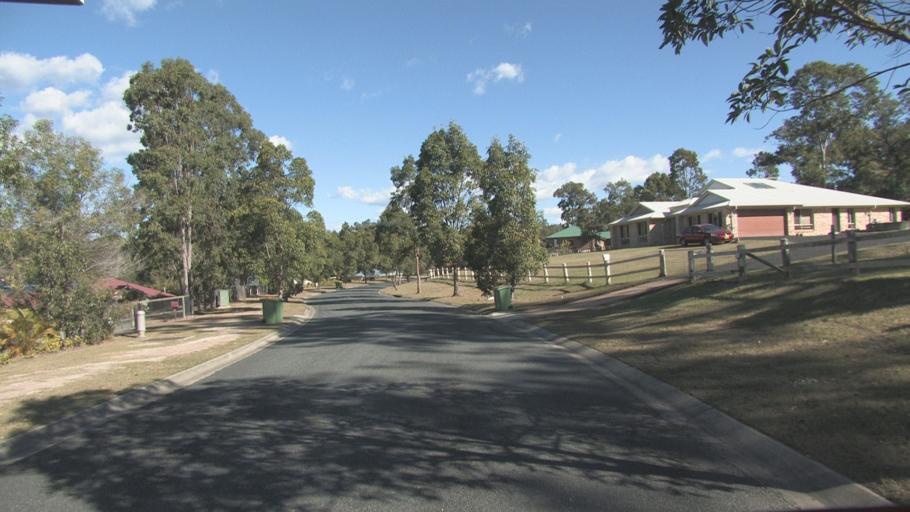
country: AU
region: Queensland
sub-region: Ipswich
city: Springfield Lakes
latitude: -27.7337
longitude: 152.9133
